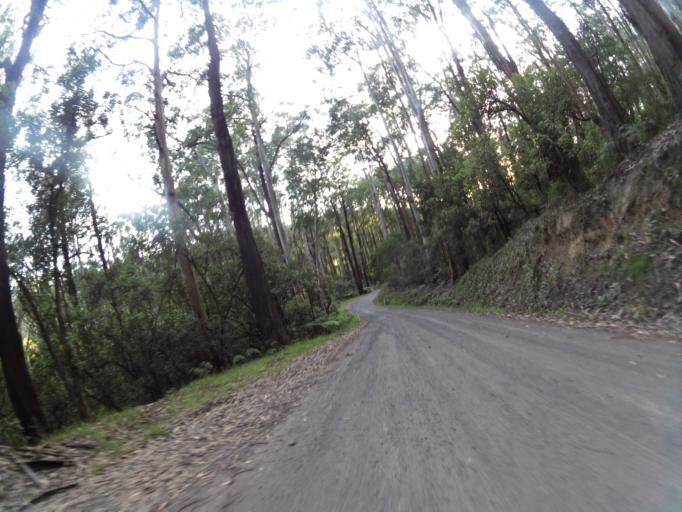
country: AU
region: Victoria
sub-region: Colac-Otway
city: Apollo Bay
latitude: -38.5482
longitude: 143.7382
